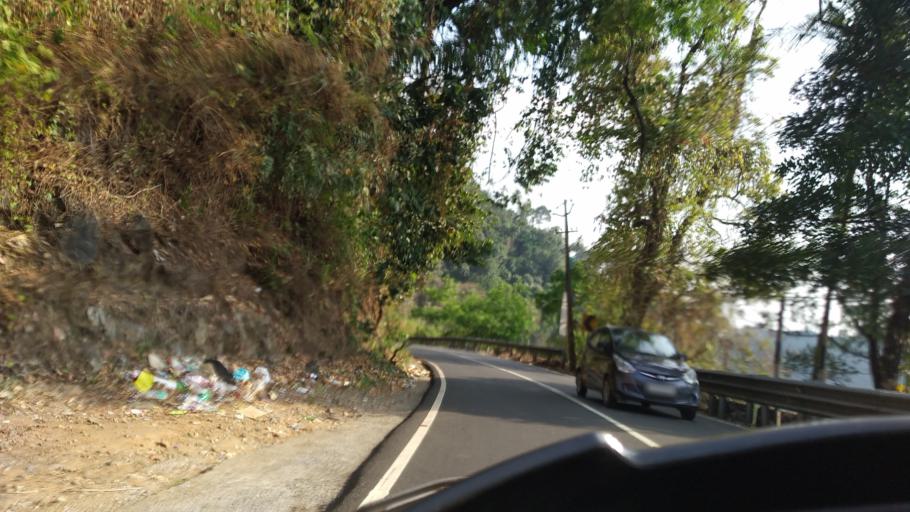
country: IN
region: Kerala
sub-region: Kottayam
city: Erattupetta
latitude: 9.5564
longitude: 76.9381
